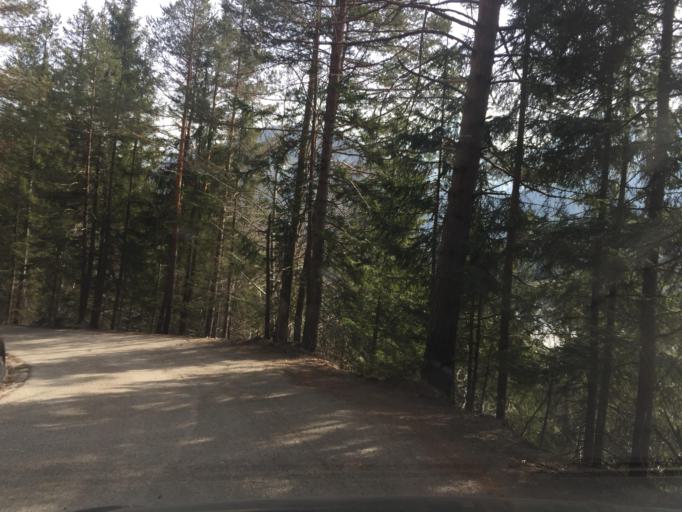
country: IT
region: Friuli Venezia Giulia
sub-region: Provincia di Udine
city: Tarvisio
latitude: 46.4989
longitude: 13.6361
